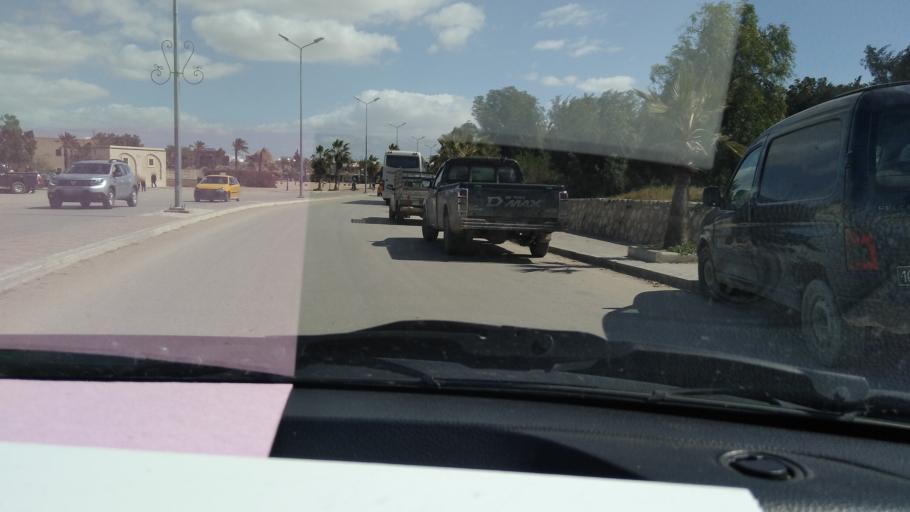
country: TN
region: Al Qayrawan
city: Kairouan
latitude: 35.6806
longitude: 10.0889
